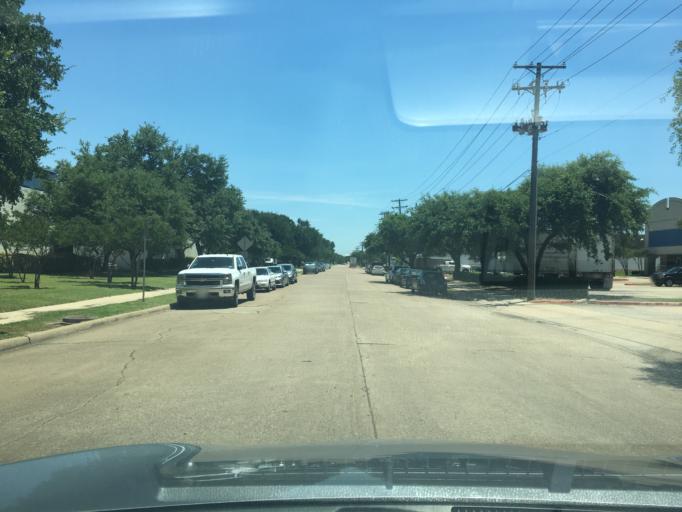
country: US
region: Texas
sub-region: Dallas County
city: Richardson
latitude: 32.9656
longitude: -96.7031
